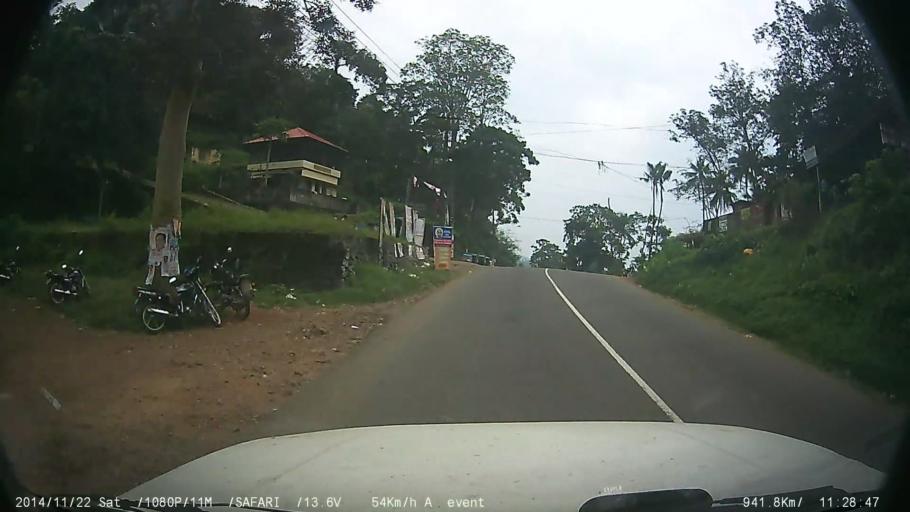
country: IN
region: Kerala
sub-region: Ernakulam
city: Muvattupuzha
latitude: 9.9270
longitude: 76.5799
